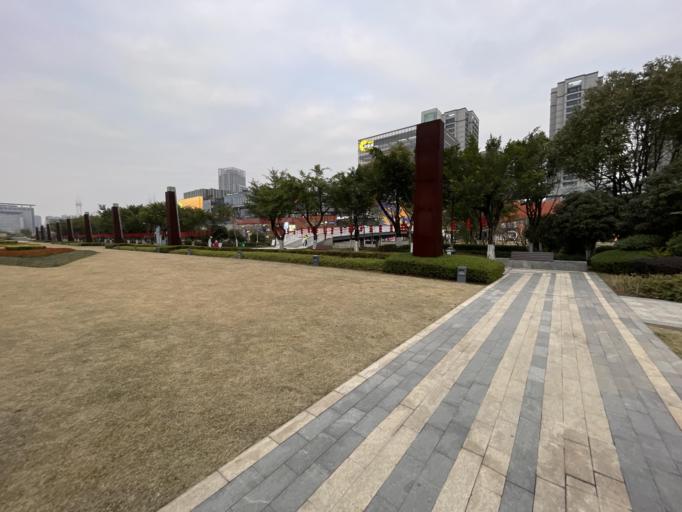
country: CN
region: Zhejiang Sheng
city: Wenzhou
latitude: 27.9868
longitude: 120.6953
